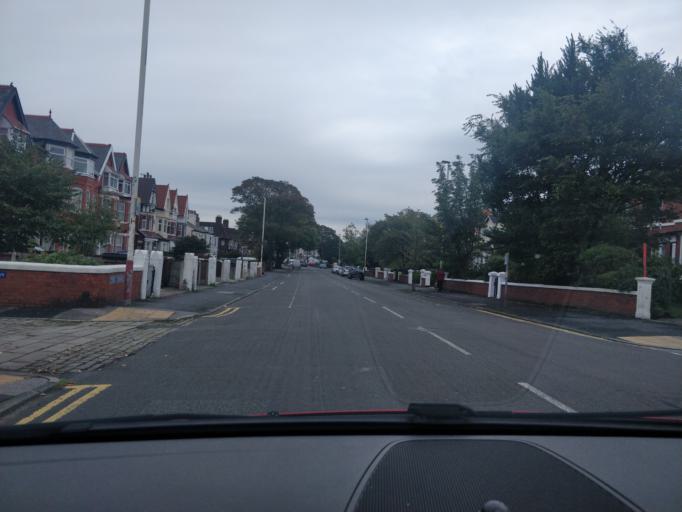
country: GB
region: England
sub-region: Sefton
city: Southport
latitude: 53.6501
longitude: -2.9949
